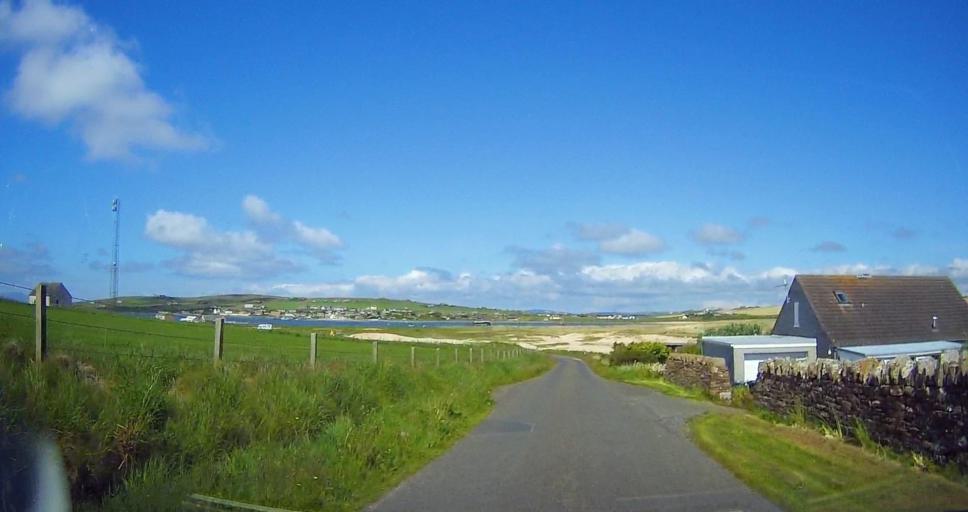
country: GB
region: Scotland
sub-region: Orkney Islands
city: Kirkwall
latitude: 58.8365
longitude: -2.9033
